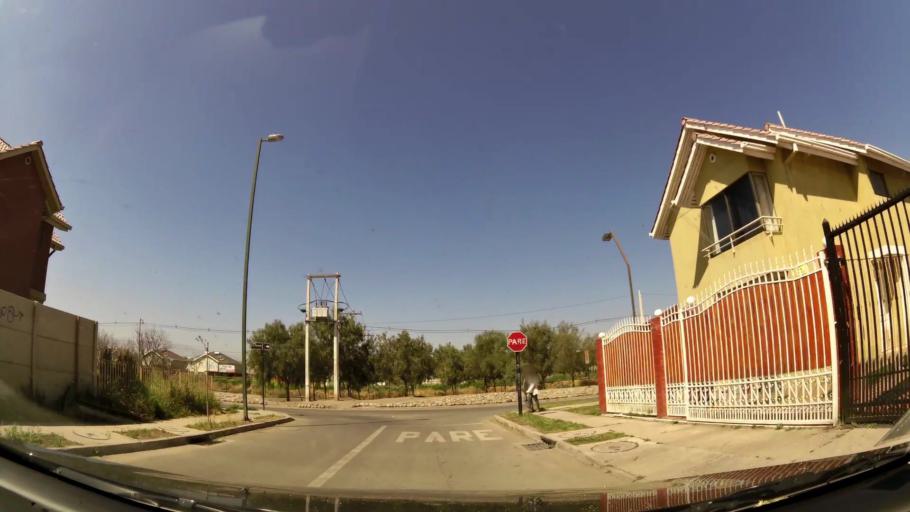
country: CL
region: Santiago Metropolitan
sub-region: Provincia de Chacabuco
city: Chicureo Abajo
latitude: -33.3255
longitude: -70.7512
